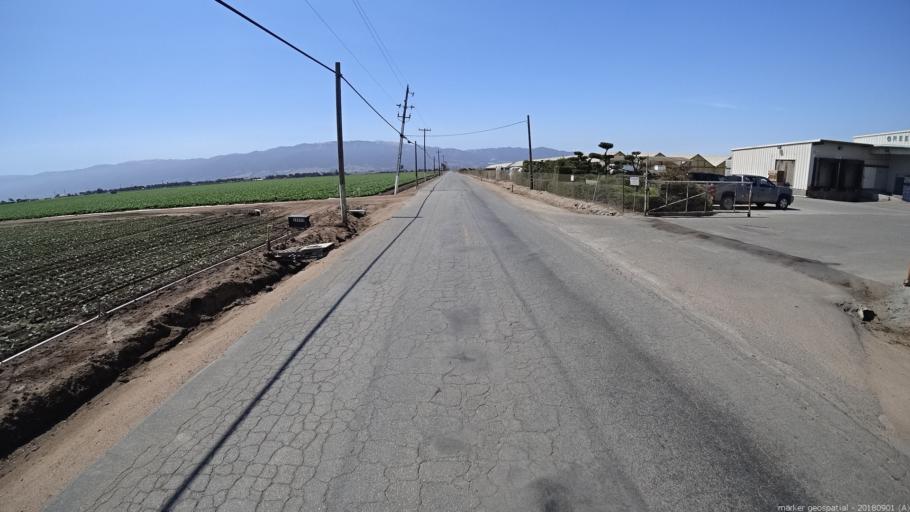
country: US
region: California
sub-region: Monterey County
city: Chualar
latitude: 36.6229
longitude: -121.5314
